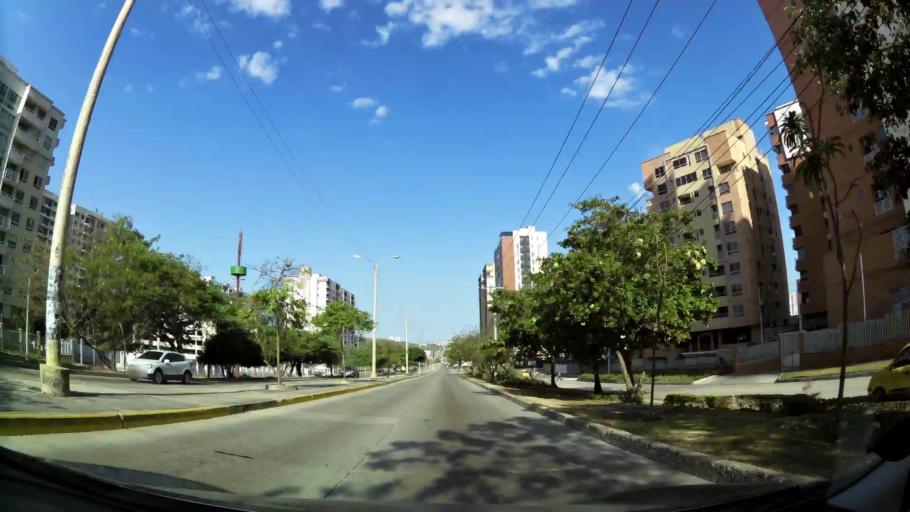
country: CO
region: Atlantico
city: Barranquilla
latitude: 11.0087
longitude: -74.8351
